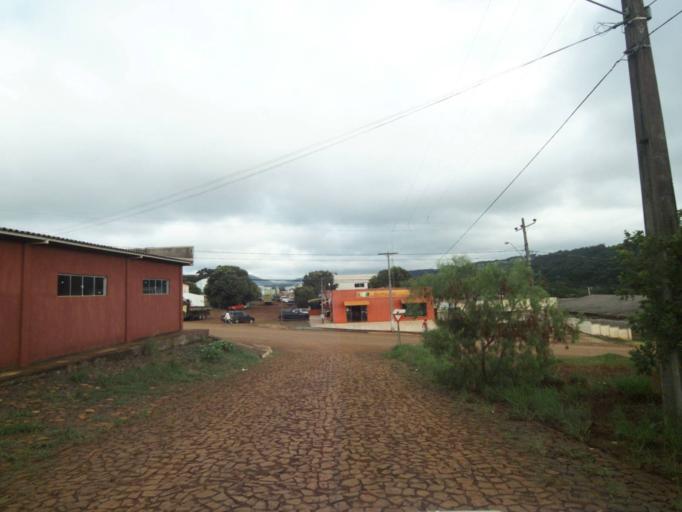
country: BR
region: Parana
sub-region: Pitanga
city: Pitanga
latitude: -24.9408
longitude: -51.8693
